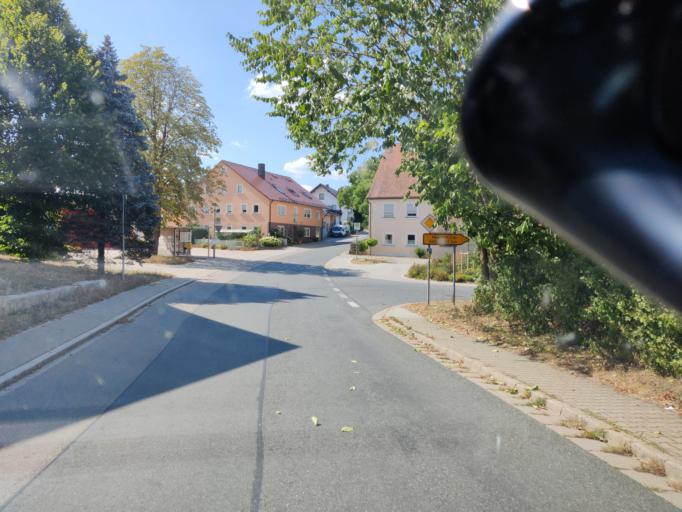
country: DE
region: Bavaria
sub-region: Regierungsbezirk Mittelfranken
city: Thalmassing
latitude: 49.0693
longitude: 11.2237
